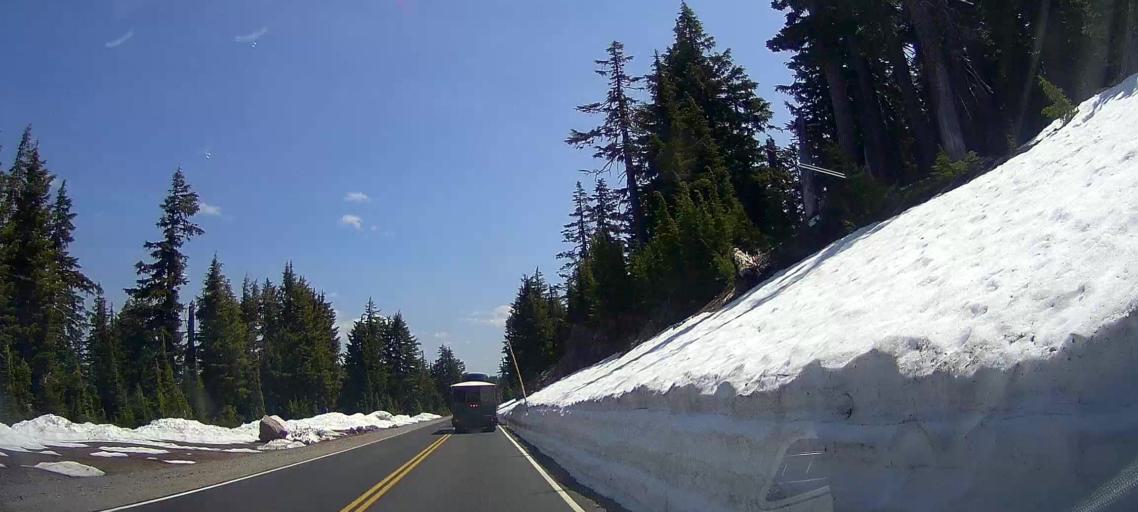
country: US
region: Oregon
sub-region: Jackson County
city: Shady Cove
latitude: 42.9811
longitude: -122.1377
